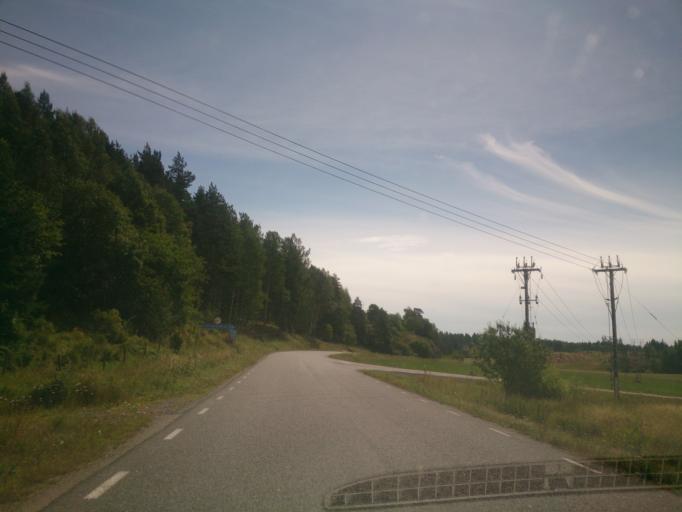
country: SE
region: OEstergoetland
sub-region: Valdemarsviks Kommun
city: Valdemarsvik
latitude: 58.2882
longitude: 16.6725
